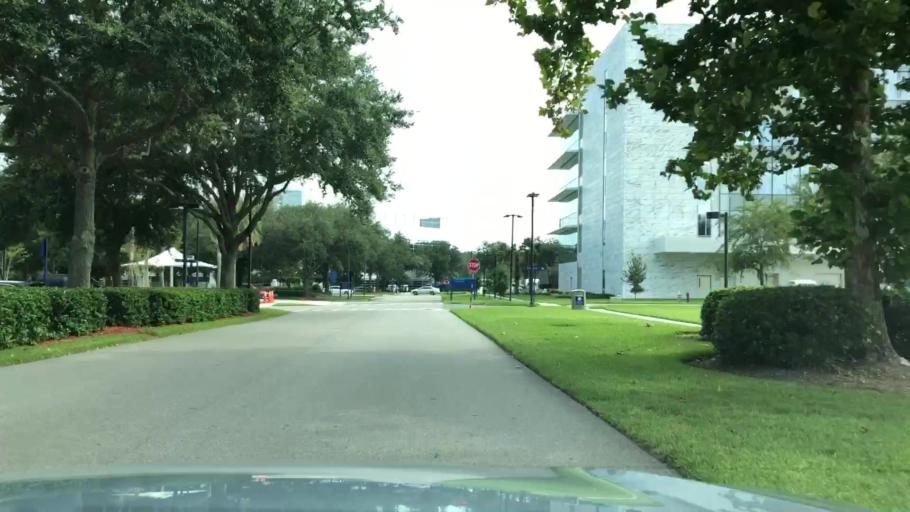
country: US
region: Florida
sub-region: Duval County
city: Jacksonville Beach
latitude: 30.2639
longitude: -81.4438
